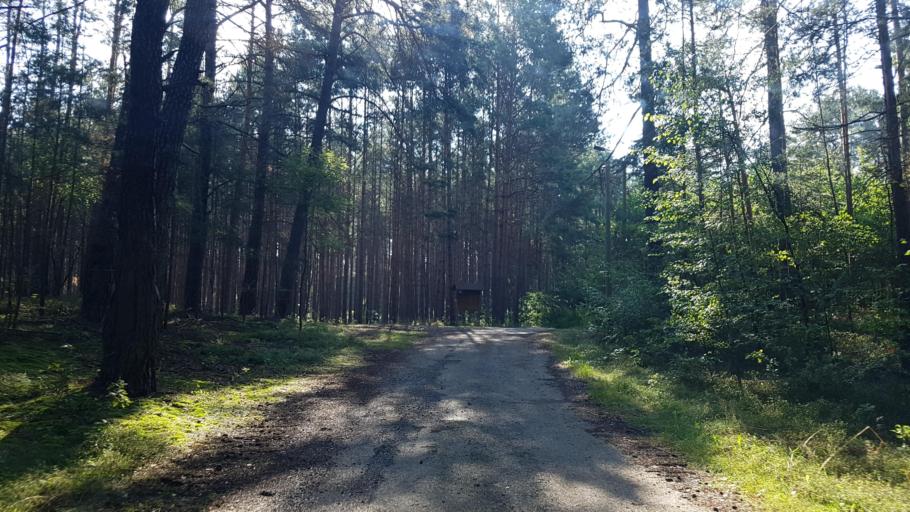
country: DE
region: Brandenburg
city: Luckau
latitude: 51.7937
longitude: 13.6375
